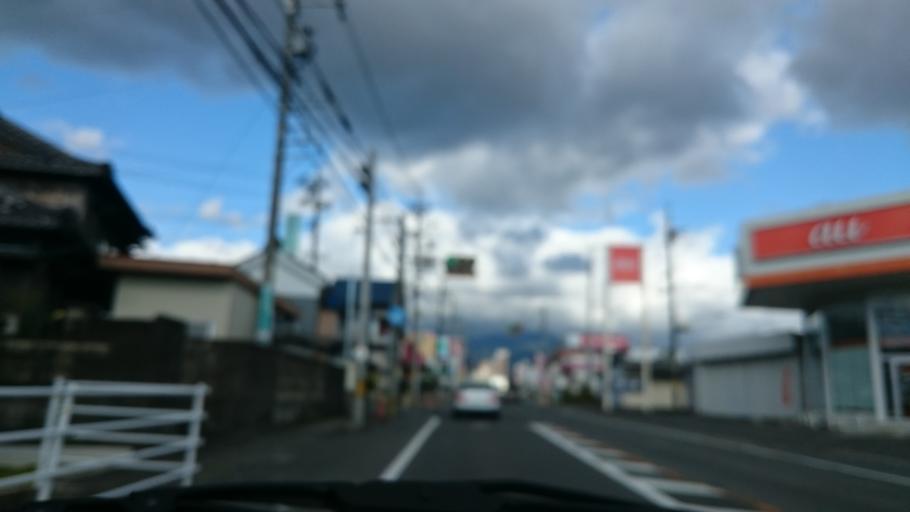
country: JP
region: Mie
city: Komono
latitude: 35.0061
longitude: 136.5235
